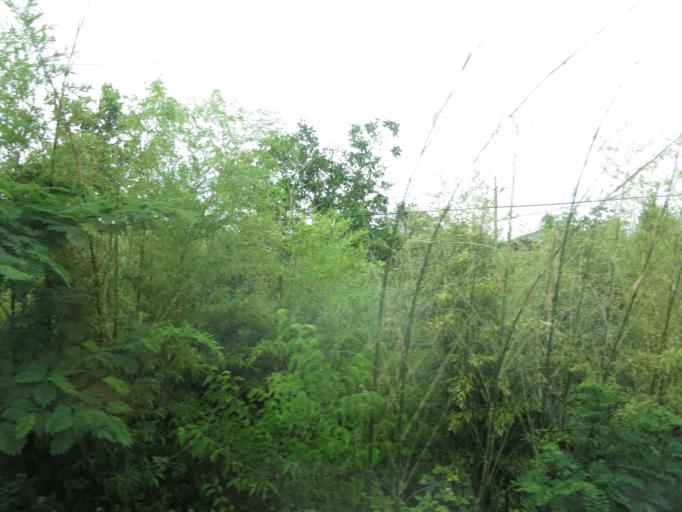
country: GE
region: Imereti
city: Samtredia
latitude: 42.1500
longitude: 42.3354
